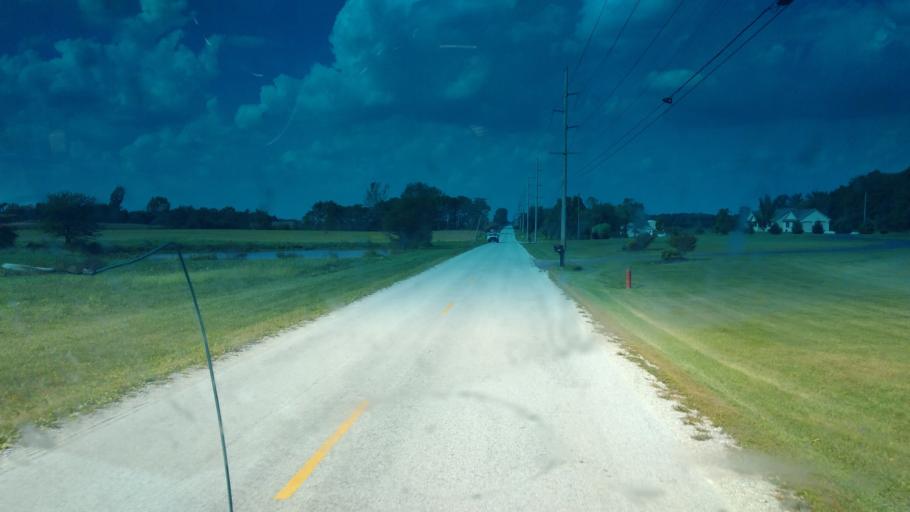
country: US
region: Ohio
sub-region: Hardin County
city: Kenton
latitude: 40.7514
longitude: -83.6524
